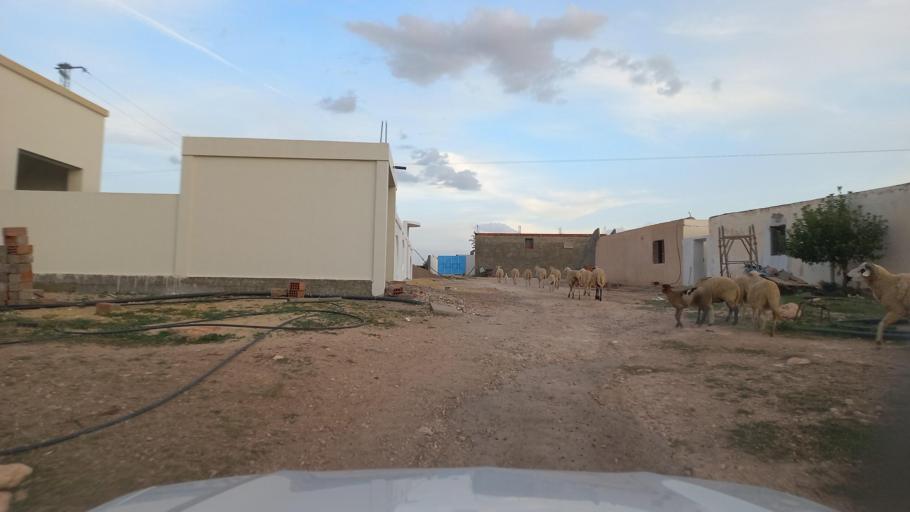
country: TN
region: Al Qasrayn
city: Sbiba
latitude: 35.4127
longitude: 9.1024
